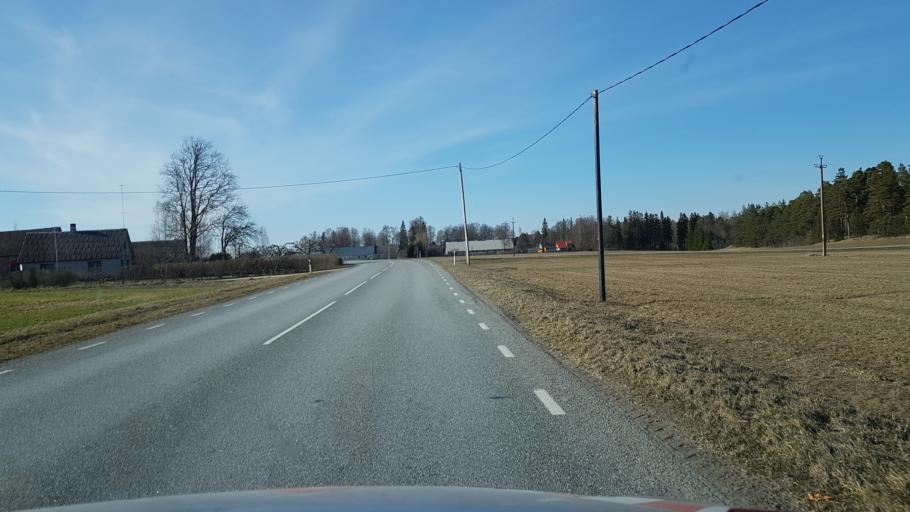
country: EE
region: Laeaene-Virumaa
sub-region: Vinni vald
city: Vinni
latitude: 59.2029
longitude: 26.5594
